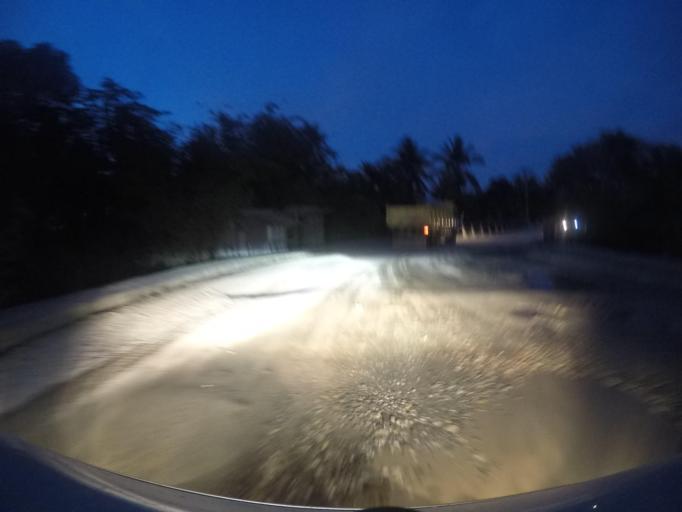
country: TL
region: Viqueque
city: Viqueque
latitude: -8.8627
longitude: 126.3627
